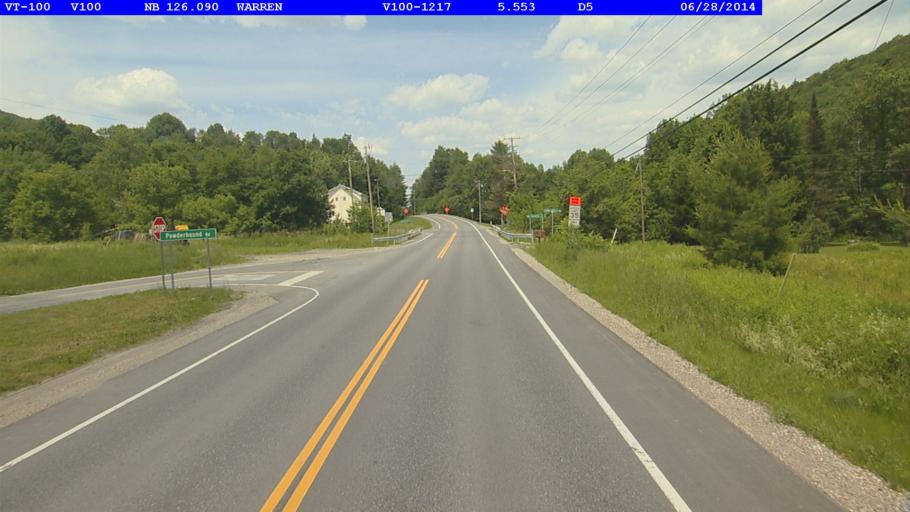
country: US
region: Vermont
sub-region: Washington County
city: Northfield
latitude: 44.1364
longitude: -72.8464
